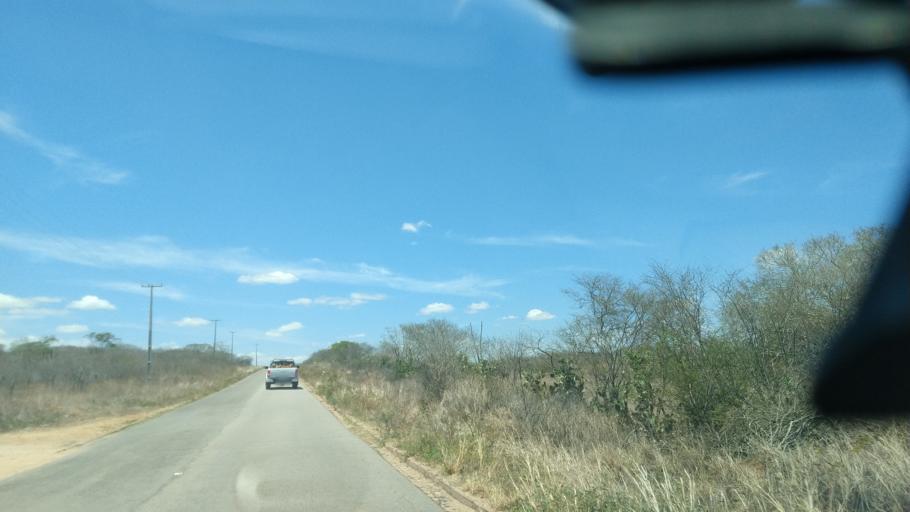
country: BR
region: Rio Grande do Norte
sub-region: Sao Paulo Do Potengi
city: Sao Paulo do Potengi
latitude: -5.9023
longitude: -35.6149
